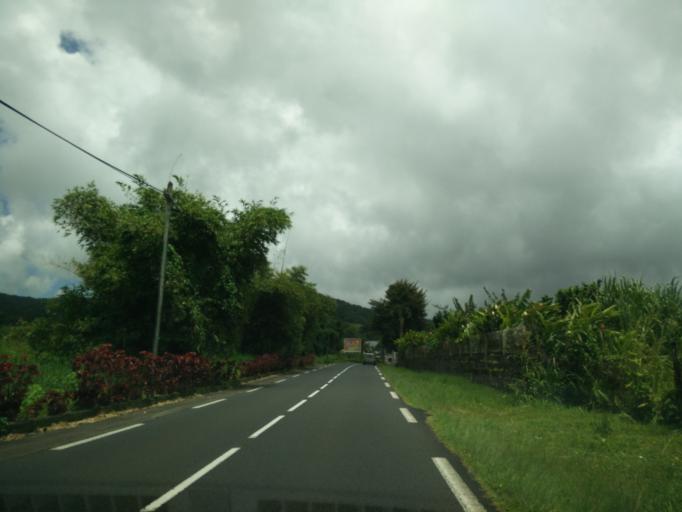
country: MQ
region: Martinique
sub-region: Martinique
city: Le Morne-Rouge
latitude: 14.7605
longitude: -61.1130
